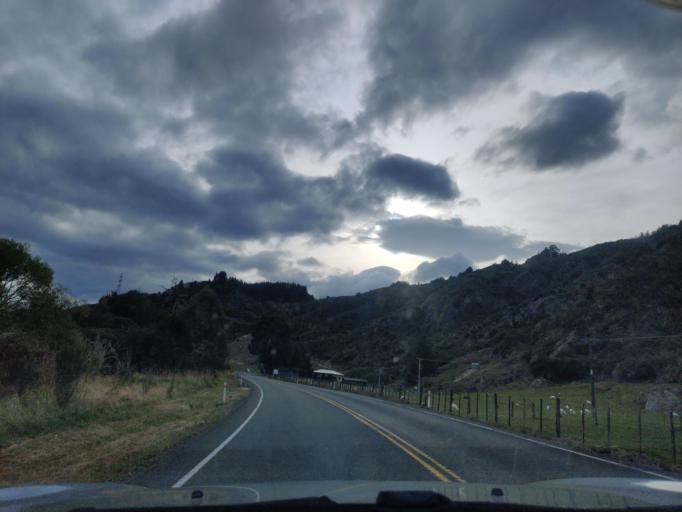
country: NZ
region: West Coast
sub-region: Buller District
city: Westport
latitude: -41.7968
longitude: 172.3615
